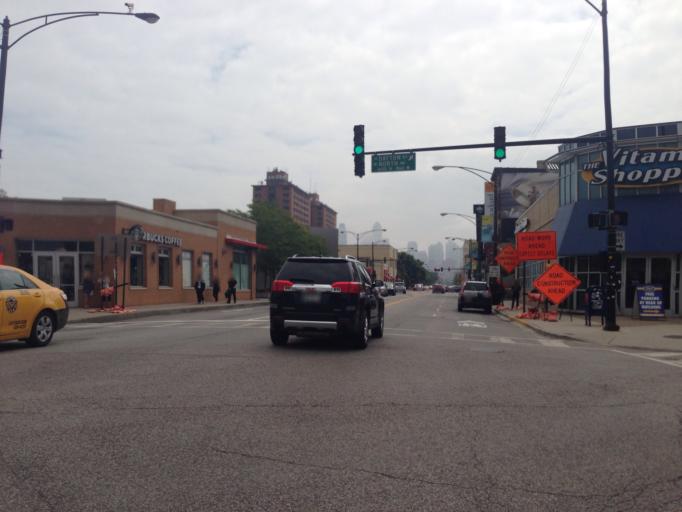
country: US
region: Illinois
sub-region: Cook County
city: Chicago
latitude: 41.9110
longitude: -87.6497
